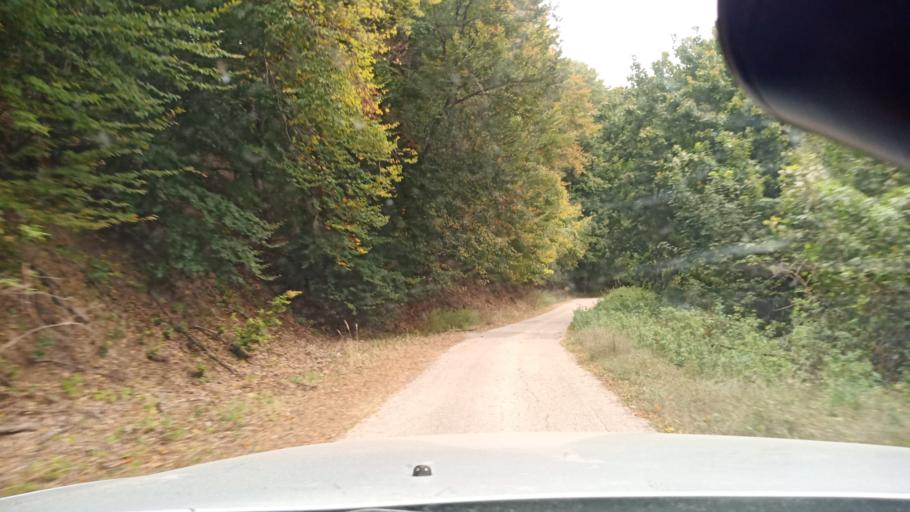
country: HU
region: Komarom-Esztergom
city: Oroszlany
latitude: 47.3965
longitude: 18.3144
